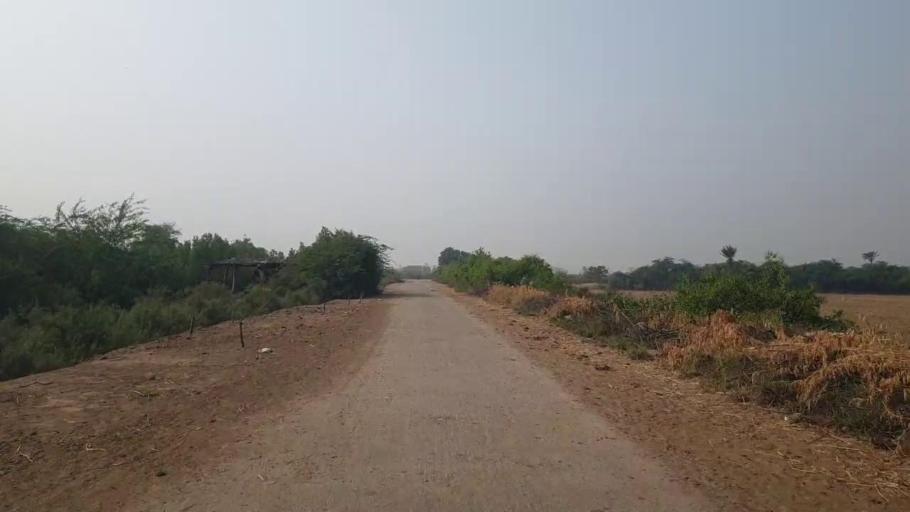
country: PK
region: Sindh
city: Tando Muhammad Khan
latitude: 25.2612
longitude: 68.4650
